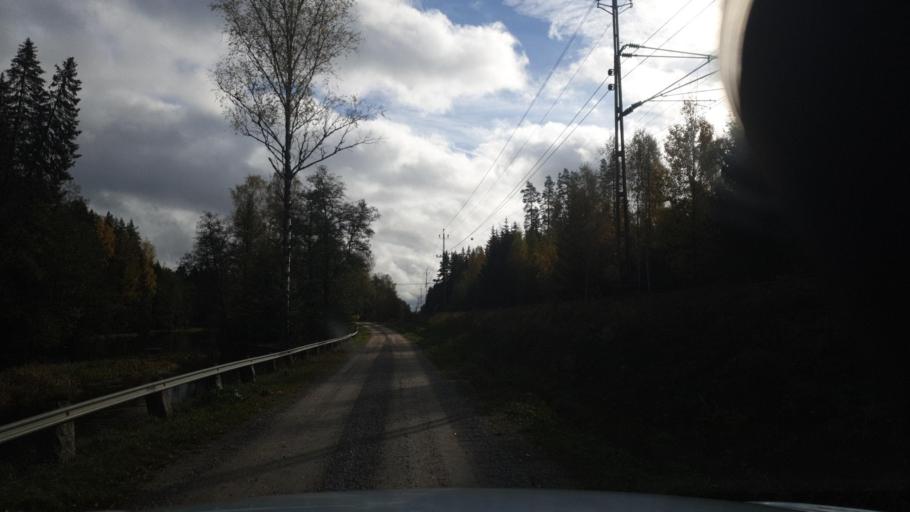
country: SE
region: Vaermland
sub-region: Karlstads Kommun
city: Edsvalla
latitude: 59.6149
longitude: 12.9715
